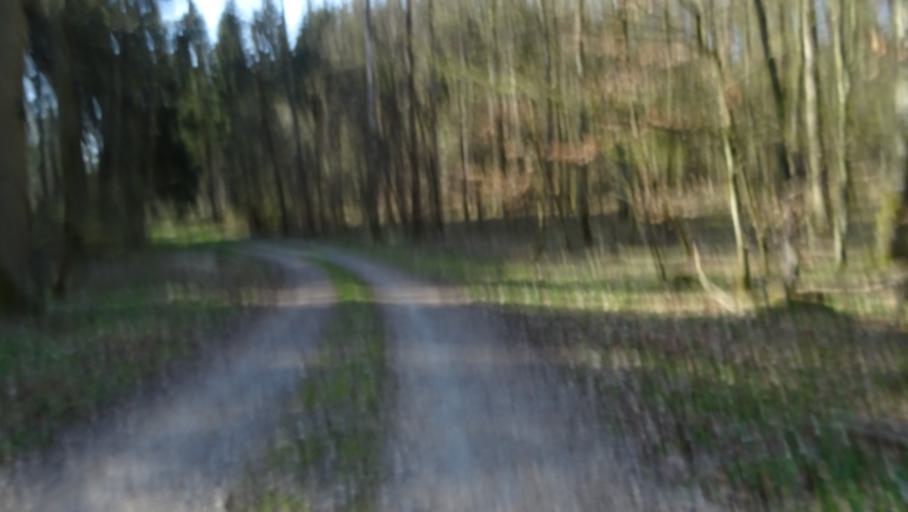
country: DE
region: Baden-Wuerttemberg
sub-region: Regierungsbezirk Stuttgart
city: Roigheim
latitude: 49.3965
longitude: 9.3112
